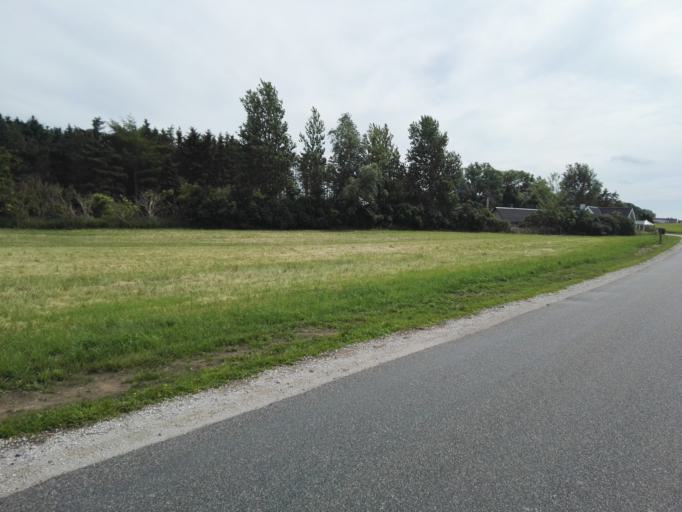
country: DK
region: Capital Region
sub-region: Hillerod Kommune
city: Skaevinge
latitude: 55.8873
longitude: 12.1303
